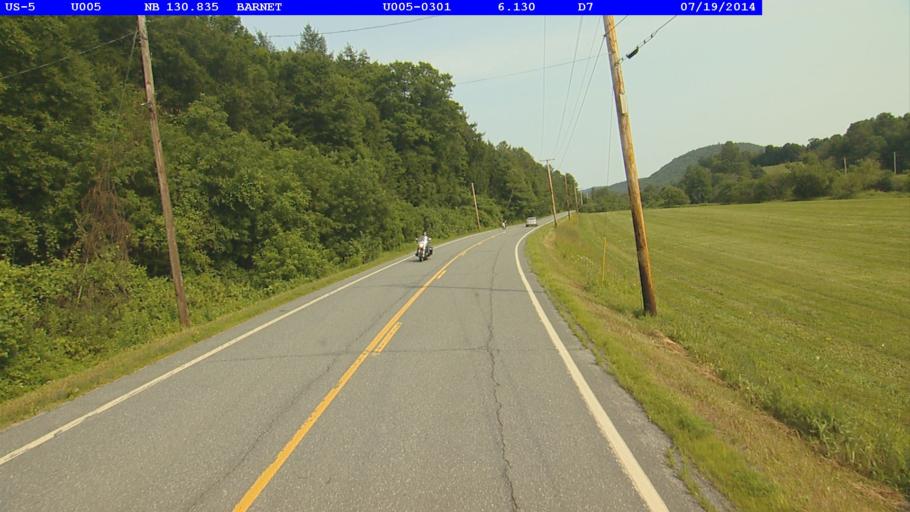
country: US
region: Vermont
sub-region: Caledonia County
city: Saint Johnsbury
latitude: 44.3325
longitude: -72.0418
